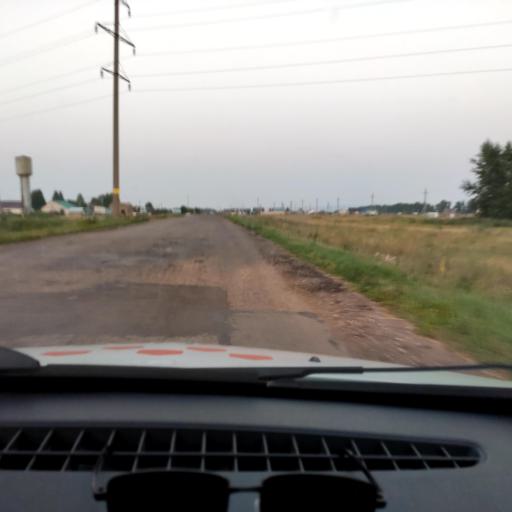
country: RU
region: Bashkortostan
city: Ulukulevo
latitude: 54.3701
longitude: 56.4241
